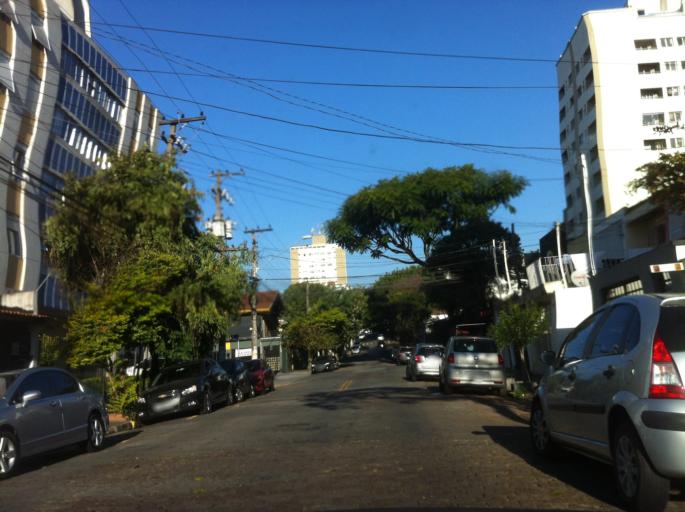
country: BR
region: Sao Paulo
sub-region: Sao Paulo
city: Sao Paulo
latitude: -23.6134
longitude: -46.6614
